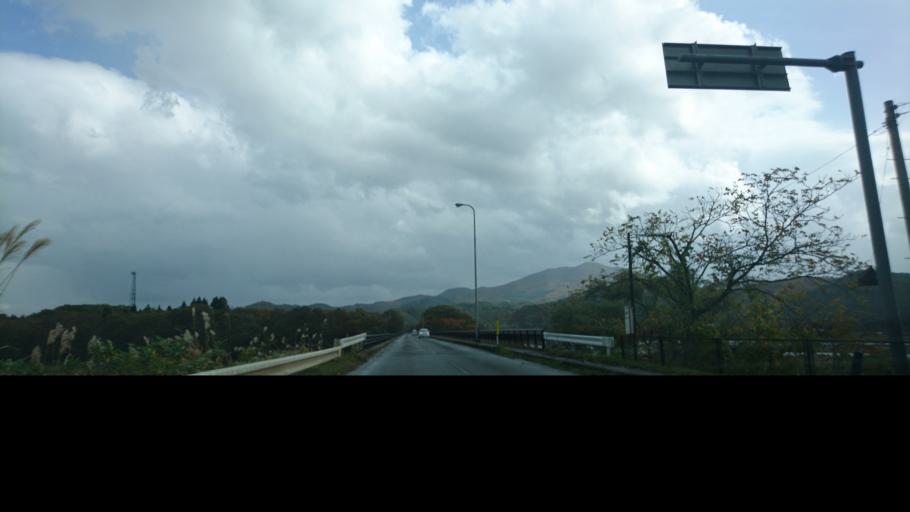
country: JP
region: Iwate
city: Shizukuishi
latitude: 39.6764
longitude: 140.9933
